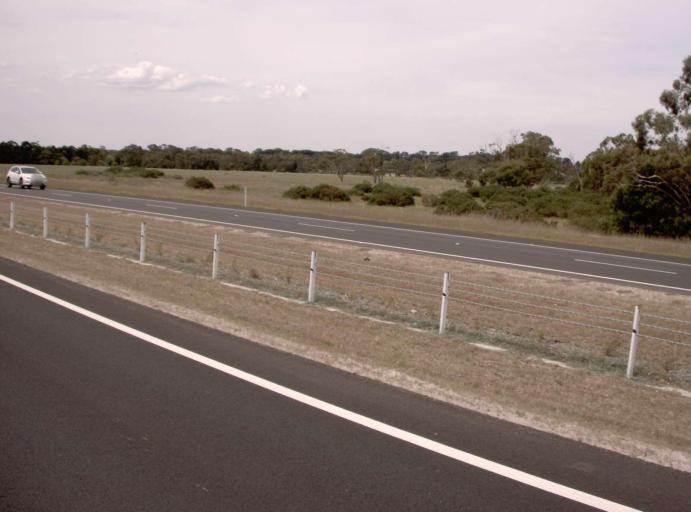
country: AU
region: Victoria
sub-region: Mornington Peninsula
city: Moorooduc
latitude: -38.2581
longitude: 145.1130
